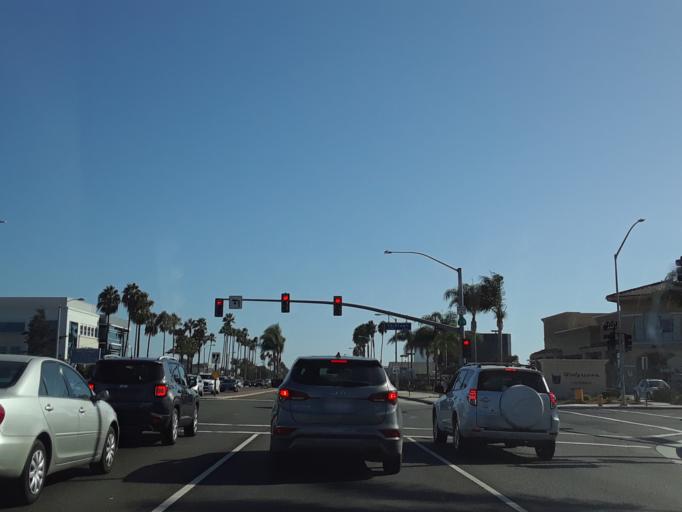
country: US
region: California
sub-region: Orange County
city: Huntington Beach
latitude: 33.6798
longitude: -117.9888
